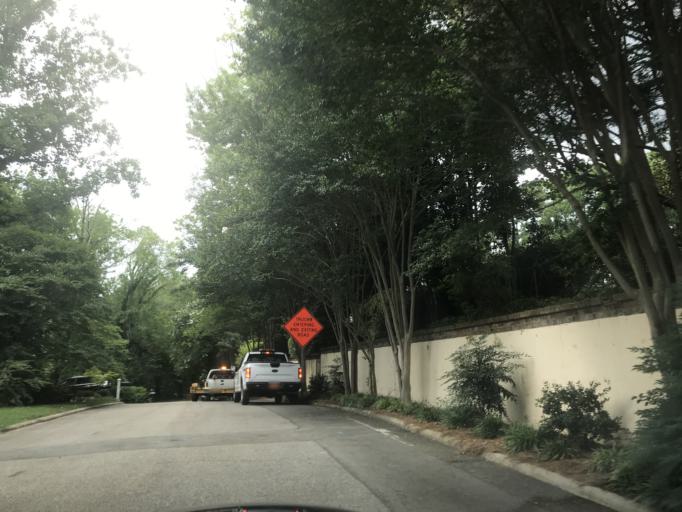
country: US
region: North Carolina
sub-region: Wake County
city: West Raleigh
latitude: 35.8279
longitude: -78.6498
